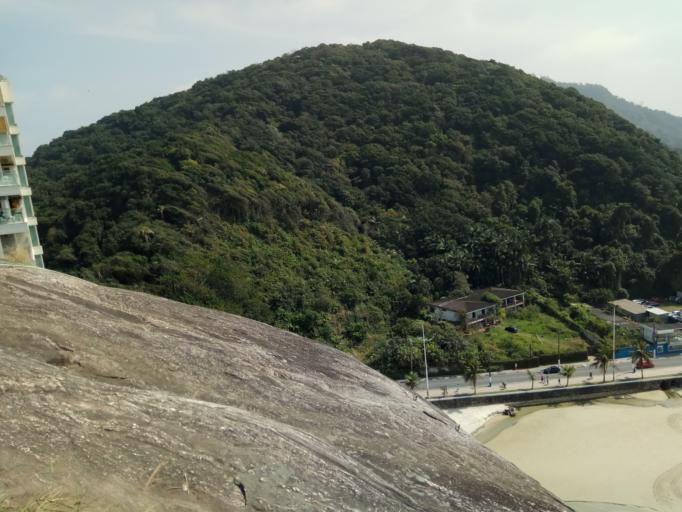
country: BR
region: Sao Paulo
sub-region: Guaruja
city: Guaruja
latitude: -23.9942
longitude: -46.2484
